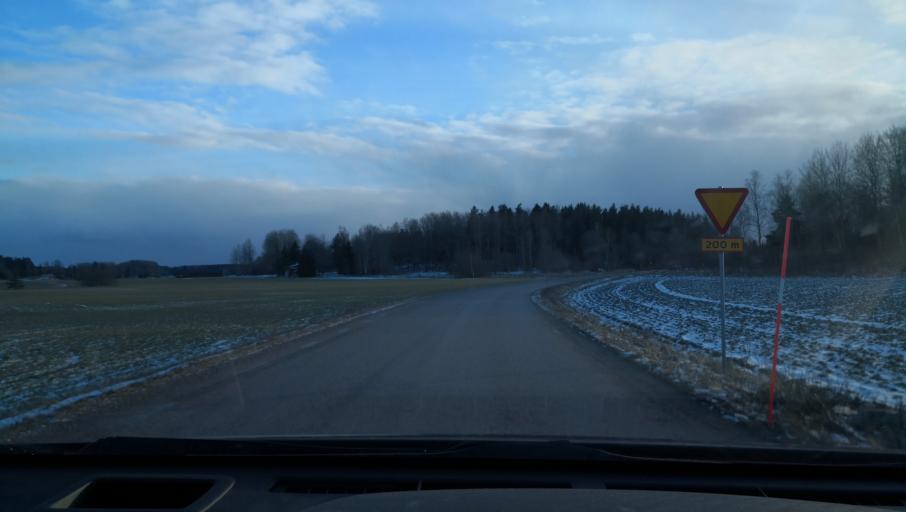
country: SE
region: Vaestmanland
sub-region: Vasteras
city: Tillberga
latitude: 59.6523
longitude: 16.7539
